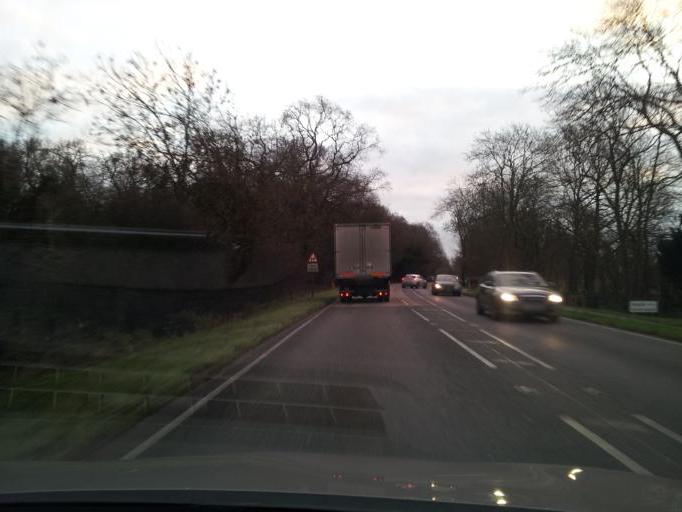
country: GB
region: England
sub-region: Cambridgeshire
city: Barton
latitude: 52.2154
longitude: 0.0460
